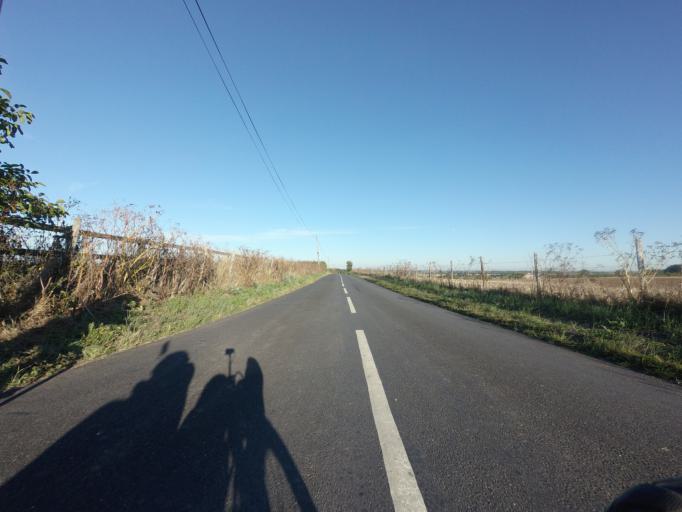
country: GB
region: England
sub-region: Kent
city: Herne Bay
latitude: 51.3505
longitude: 1.1805
